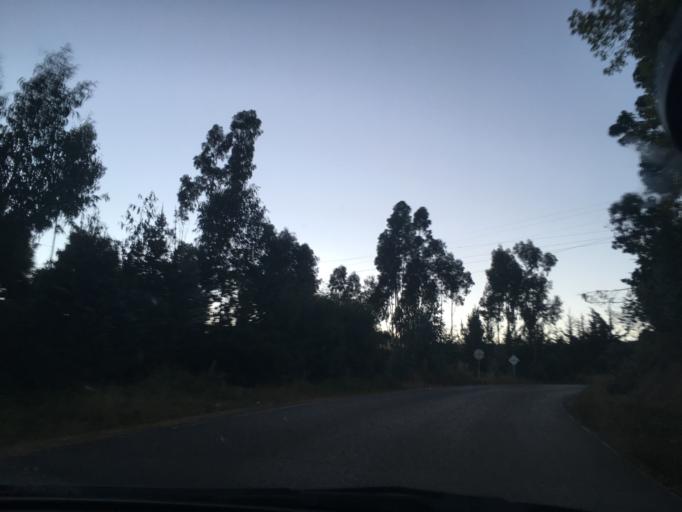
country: CO
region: Boyaca
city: Aquitania
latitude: 5.6104
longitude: -72.9101
